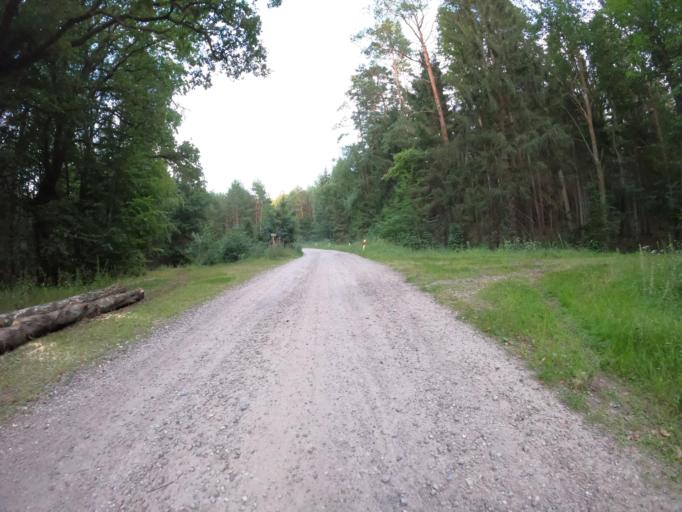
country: PL
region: West Pomeranian Voivodeship
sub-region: Powiat koszalinski
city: Sianow
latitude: 54.1005
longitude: 16.3788
